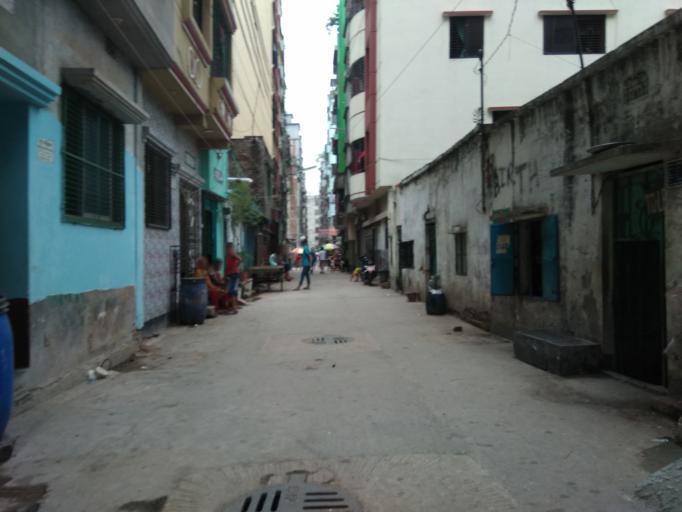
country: BD
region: Dhaka
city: Tungi
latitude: 23.8172
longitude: 90.3623
